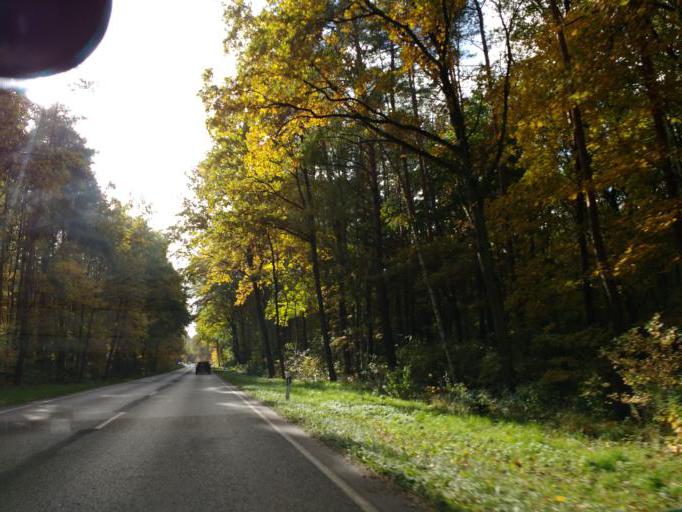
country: DE
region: Brandenburg
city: Petershagen
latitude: 52.5259
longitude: 13.8160
